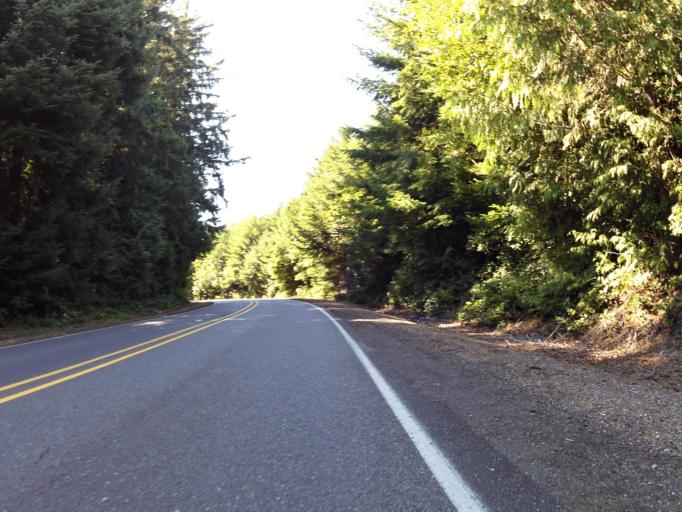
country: US
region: Oregon
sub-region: Coos County
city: Barview
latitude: 43.2411
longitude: -124.3377
